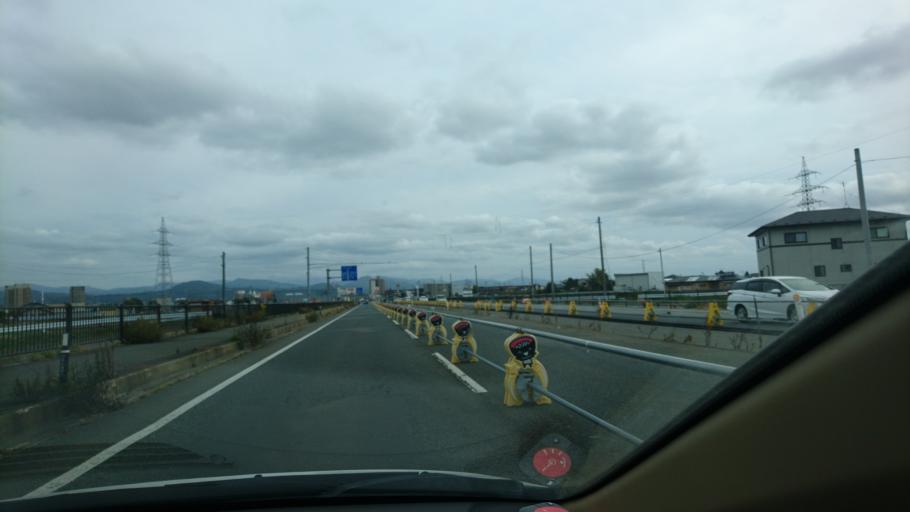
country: JP
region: Iwate
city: Morioka-shi
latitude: 39.6877
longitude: 141.1163
